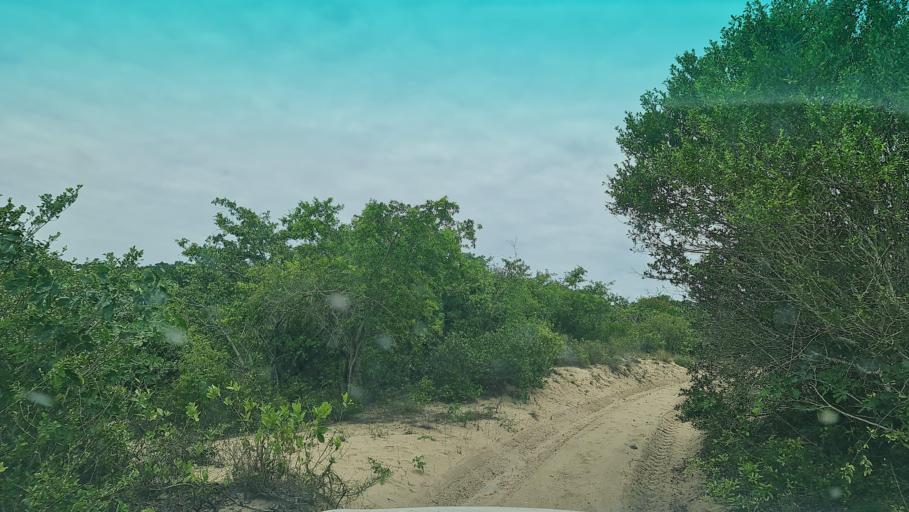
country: MZ
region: Maputo
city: Manhica
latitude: -25.6377
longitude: 32.7754
